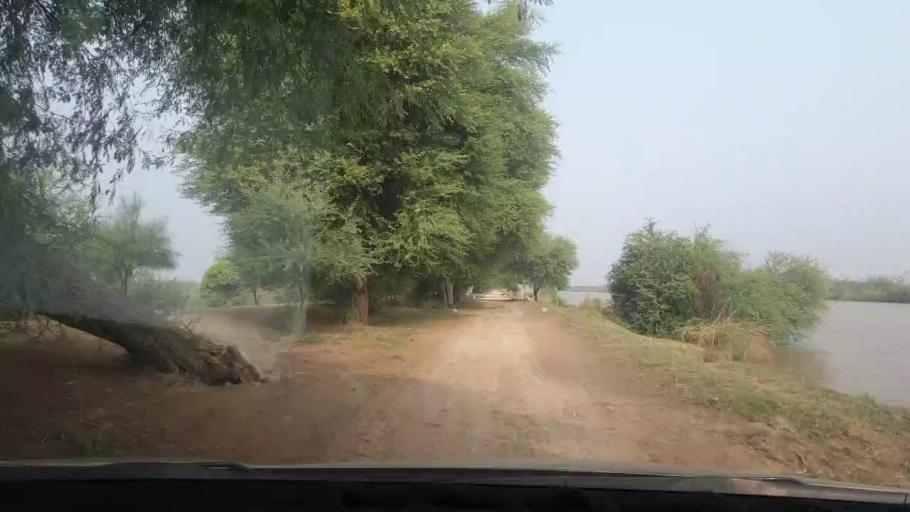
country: PK
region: Sindh
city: Tando Adam
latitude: 25.6770
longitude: 68.5572
